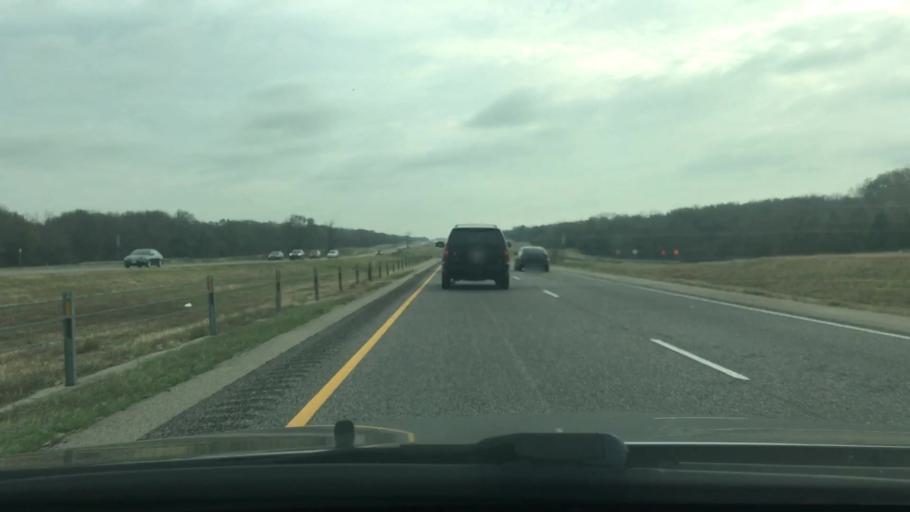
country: US
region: Texas
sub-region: Freestone County
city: Fairfield
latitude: 31.6295
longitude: -96.1579
